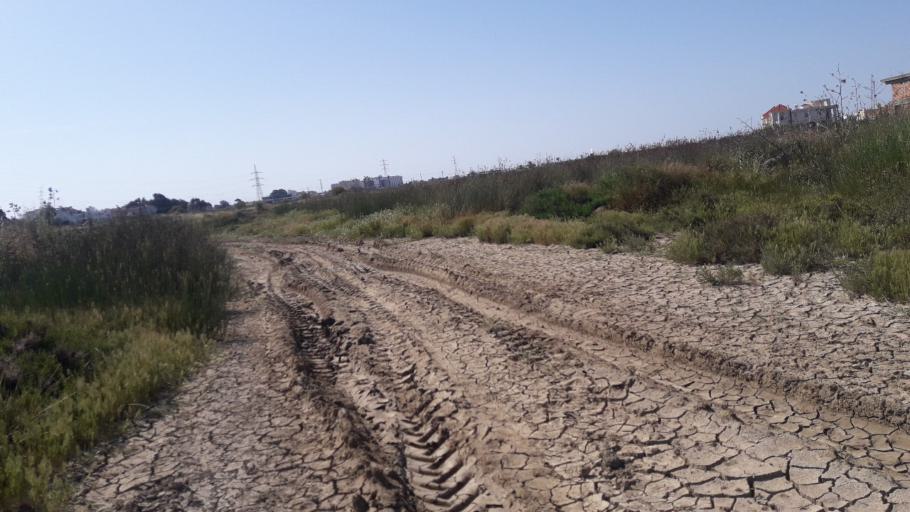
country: CY
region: Ammochostos
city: Famagusta
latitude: 35.1647
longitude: 33.8962
